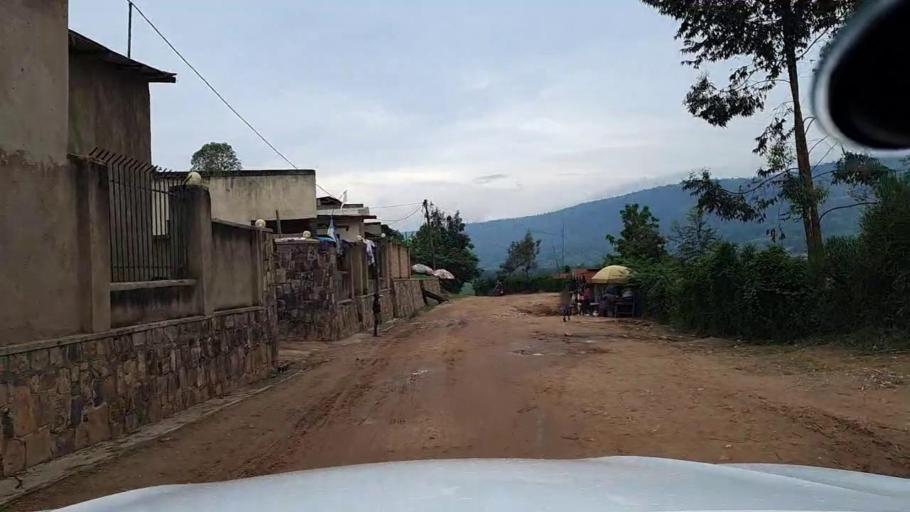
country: RW
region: Kigali
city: Kigali
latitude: -1.9575
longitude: 29.9959
